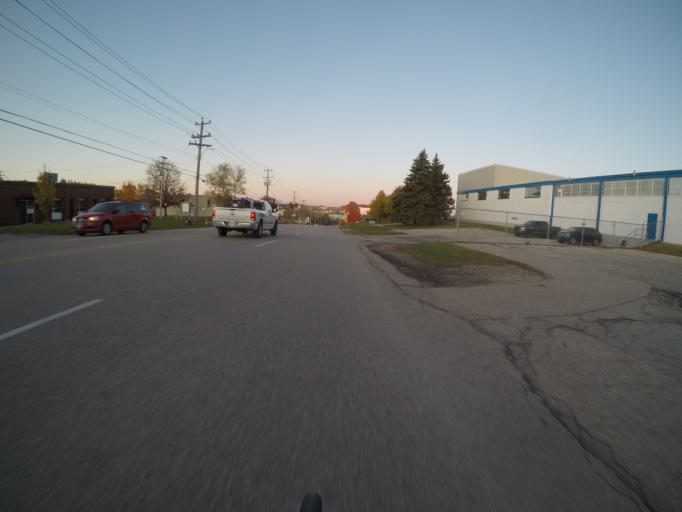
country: CA
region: Ontario
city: Kitchener
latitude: 43.4093
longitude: -80.4416
